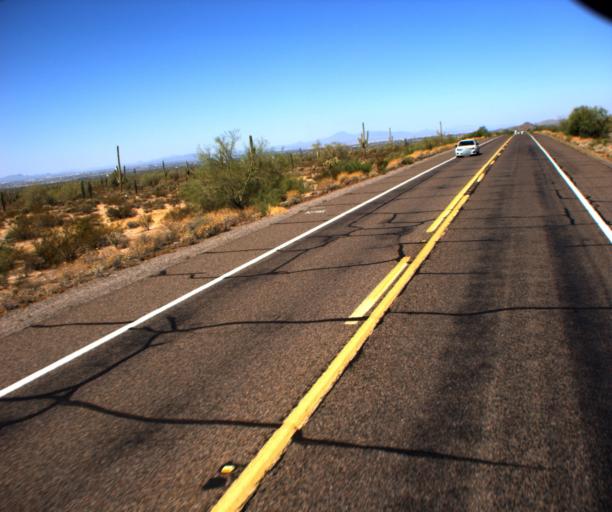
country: US
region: Arizona
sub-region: Pinal County
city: Sacaton
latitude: 33.0097
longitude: -111.6943
